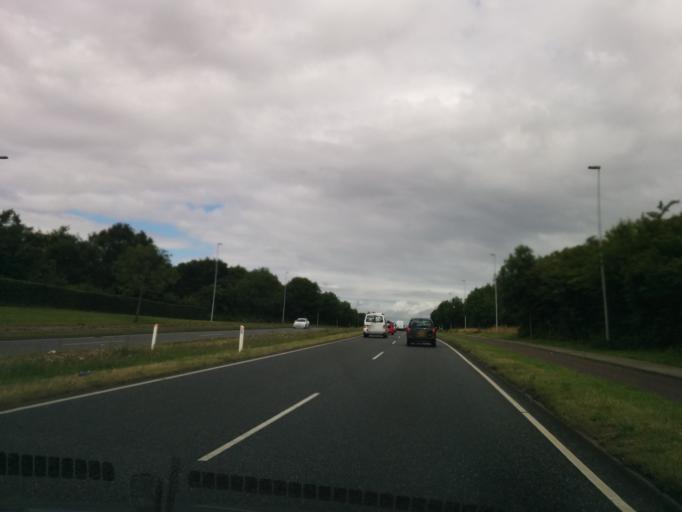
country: DK
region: Central Jutland
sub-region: Arhus Kommune
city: Arhus
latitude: 56.1881
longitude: 10.1932
